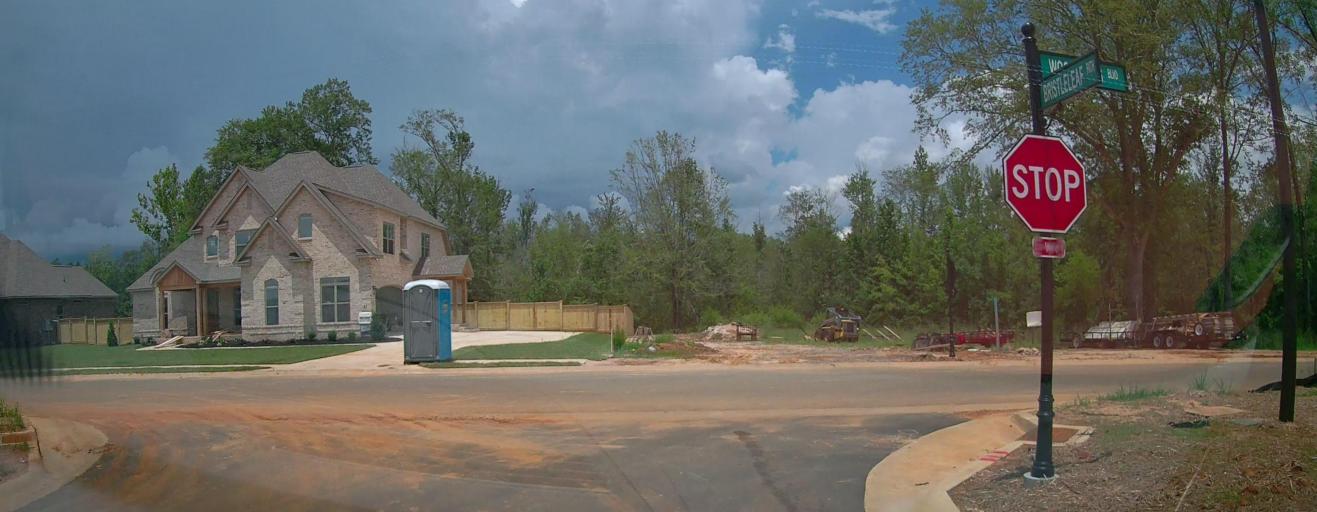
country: US
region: Georgia
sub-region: Houston County
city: Robins Air Force Base
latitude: 32.5137
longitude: -83.6234
